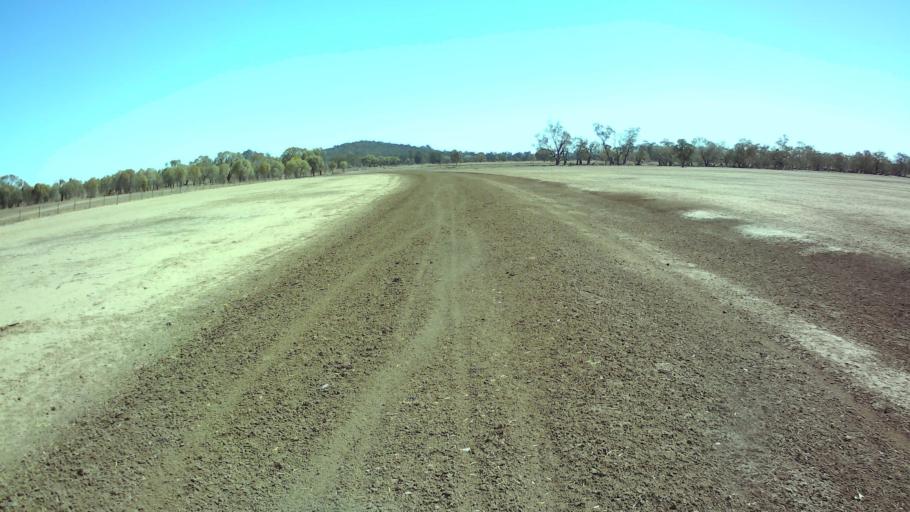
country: AU
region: New South Wales
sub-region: Bland
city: West Wyalong
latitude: -33.7528
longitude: 147.6595
